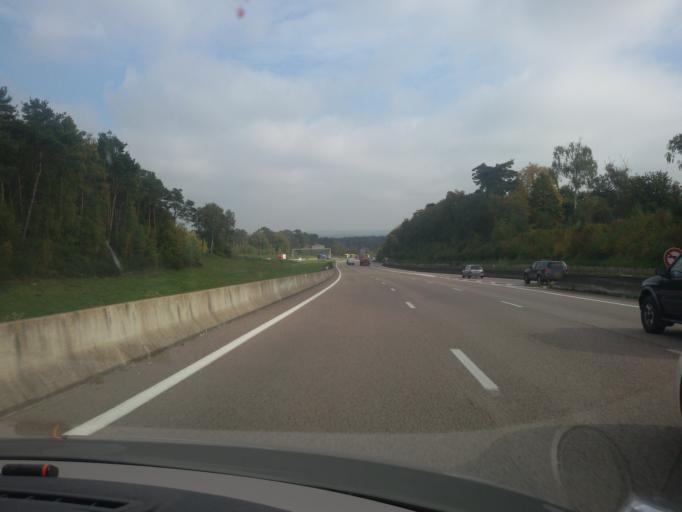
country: FR
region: Haute-Normandie
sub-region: Departement de la Seine-Maritime
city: Cleon
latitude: 49.3434
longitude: 1.0527
